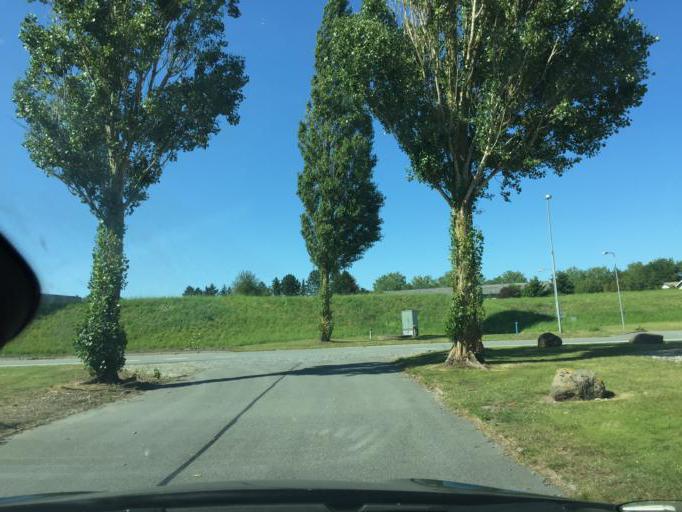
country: DK
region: South Denmark
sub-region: Nordfyns Kommune
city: Sonderso
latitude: 55.4777
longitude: 10.2641
